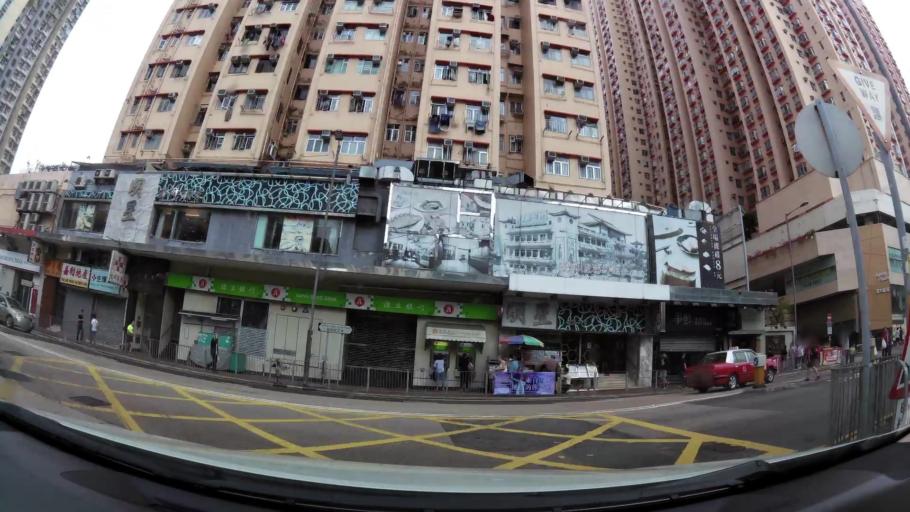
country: HK
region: Kowloon City
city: Kowloon
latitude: 22.3233
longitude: 114.2168
